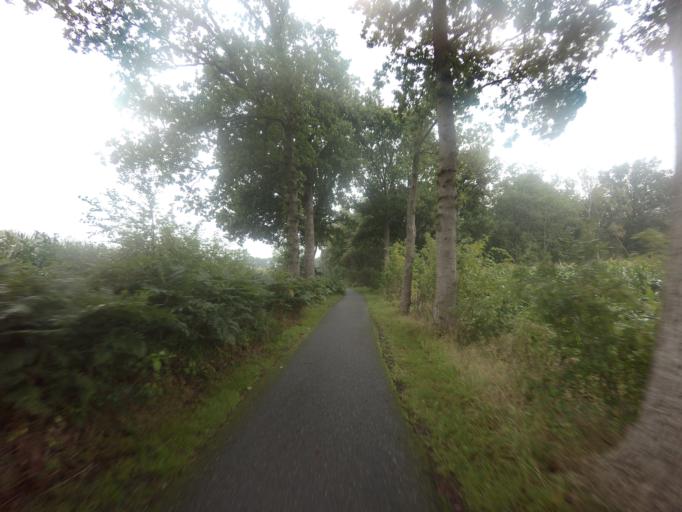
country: NL
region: Friesland
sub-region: Gemeente Heerenveen
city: Nieuwehorne
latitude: 52.9554
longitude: 6.0498
